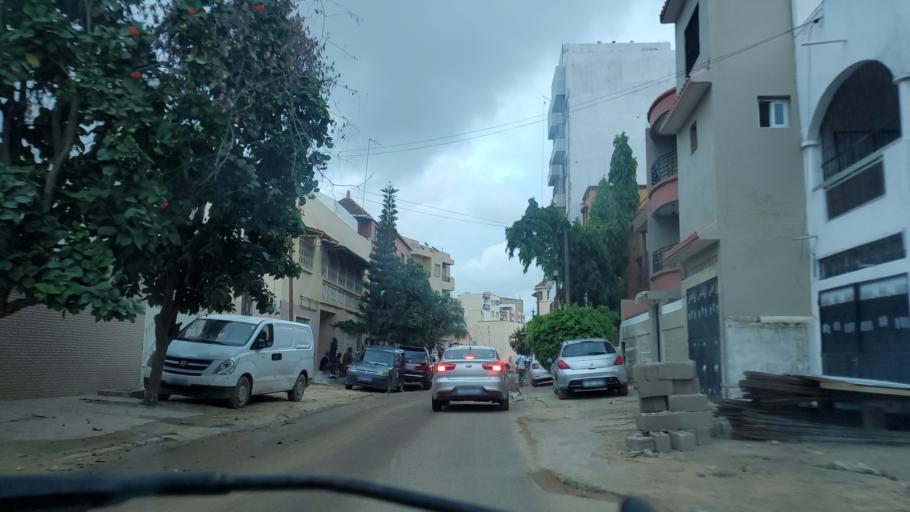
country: SN
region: Dakar
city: Mermoz Boabab
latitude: 14.7178
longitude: -17.4696
